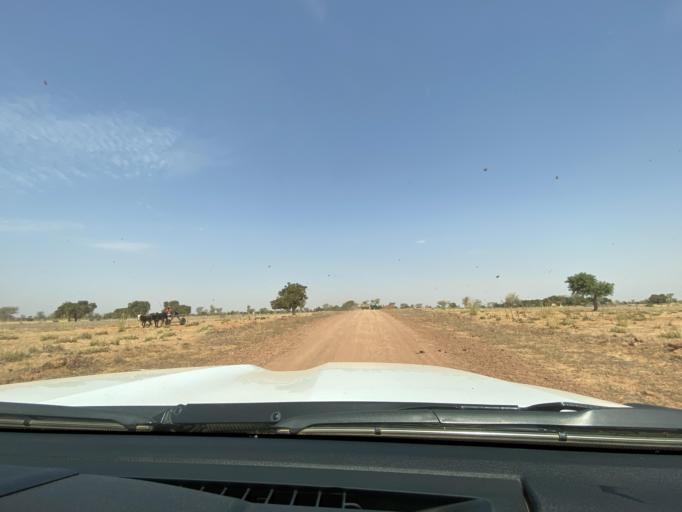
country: NE
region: Dosso
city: Birnin Gaoure
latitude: 13.2373
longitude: 2.8674
